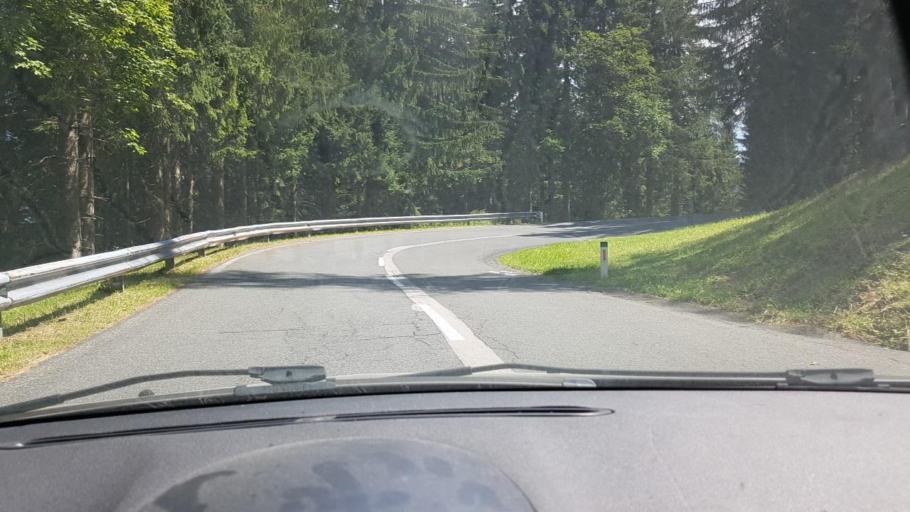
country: SI
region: Jezersko
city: Zgornje Jezersko
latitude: 46.4184
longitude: 14.5313
